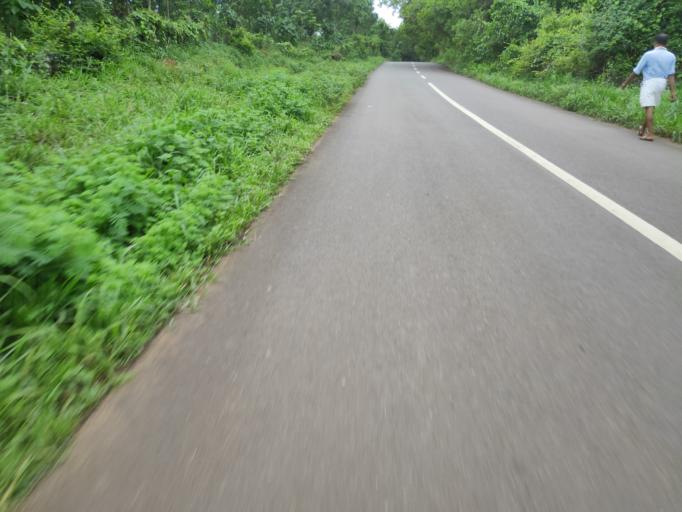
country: IN
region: Kerala
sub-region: Malappuram
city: Manjeri
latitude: 11.1708
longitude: 76.1819
